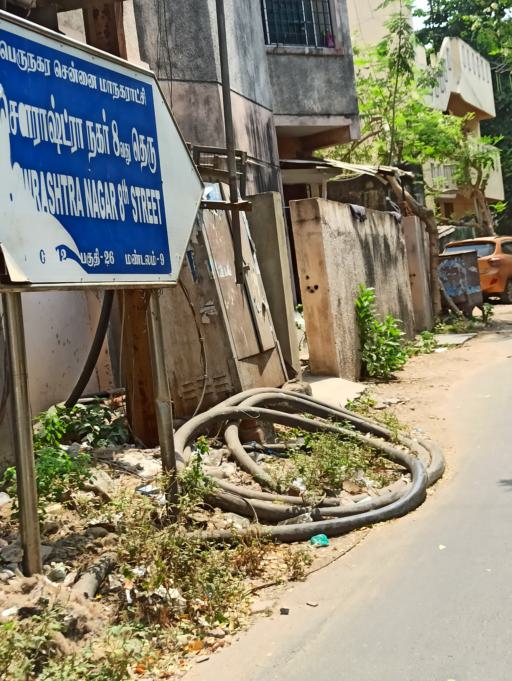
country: IN
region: Tamil Nadu
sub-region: Chennai
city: Chetput
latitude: 13.0622
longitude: 80.2321
